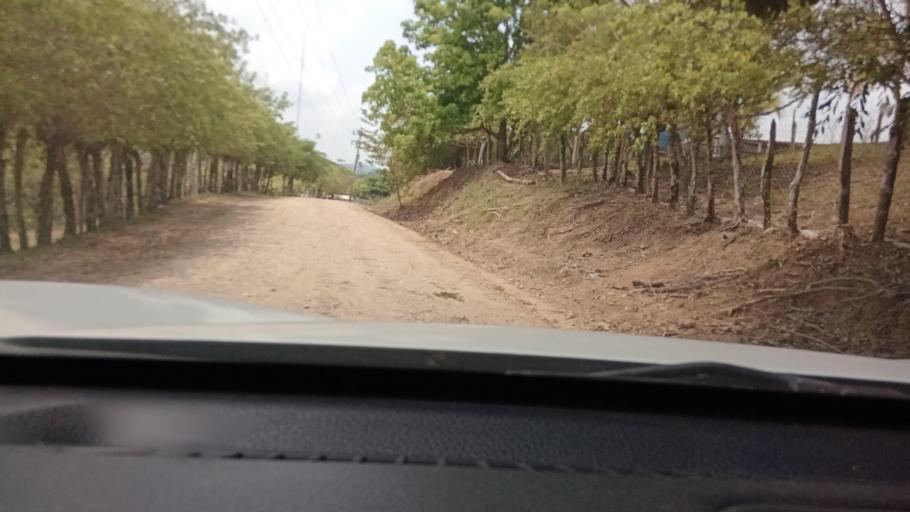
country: MX
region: Tabasco
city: Chontalpa
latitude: 17.5668
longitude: -93.7127
